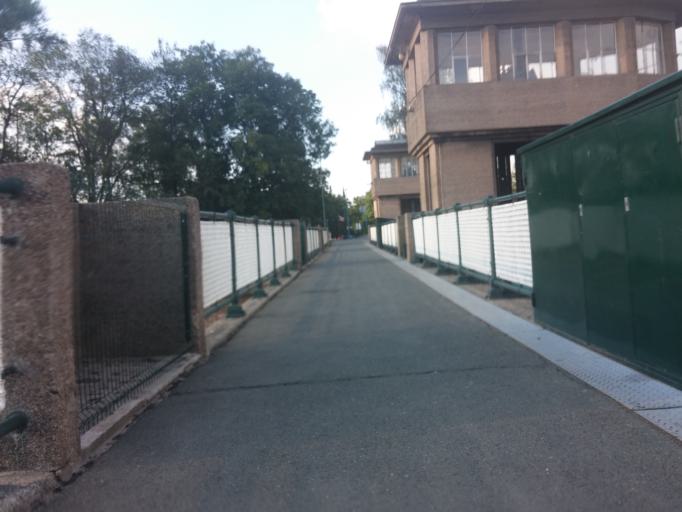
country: CZ
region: Central Bohemia
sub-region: Okres Nymburk
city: Podebrady
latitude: 50.1391
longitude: 15.1217
